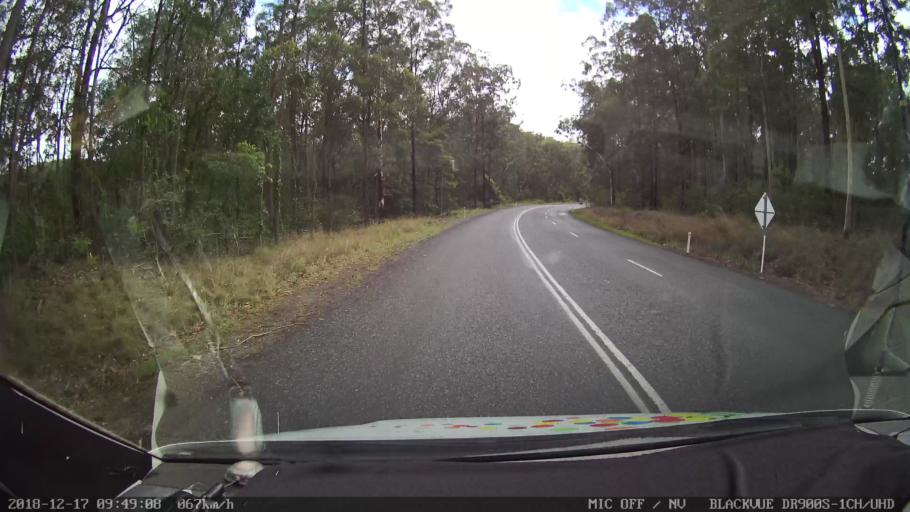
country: AU
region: New South Wales
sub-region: Tenterfield Municipality
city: Carrolls Creek
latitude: -28.9239
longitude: 152.3489
